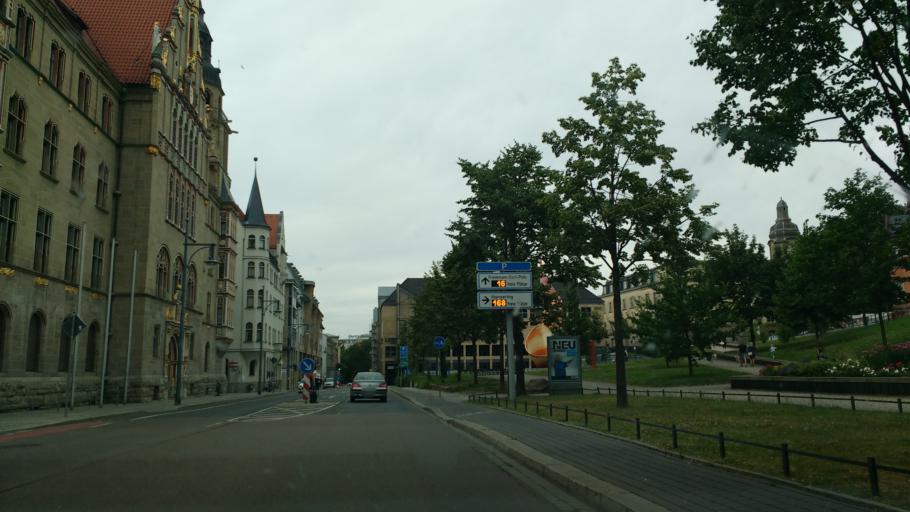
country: DE
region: Saxony-Anhalt
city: Halle (Saale)
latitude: 51.4823
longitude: 11.9749
